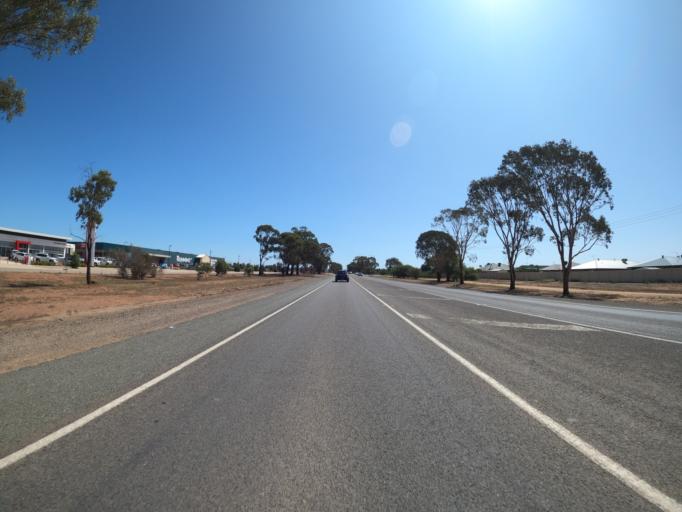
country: AU
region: Victoria
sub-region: Moira
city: Yarrawonga
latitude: -36.0108
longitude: 146.0274
